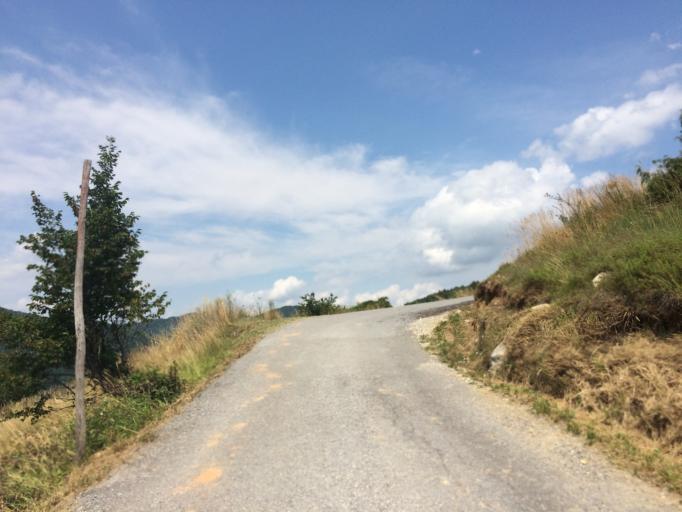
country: IT
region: Piedmont
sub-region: Provincia di Cuneo
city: Bagnasco
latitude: 44.3152
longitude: 8.0605
